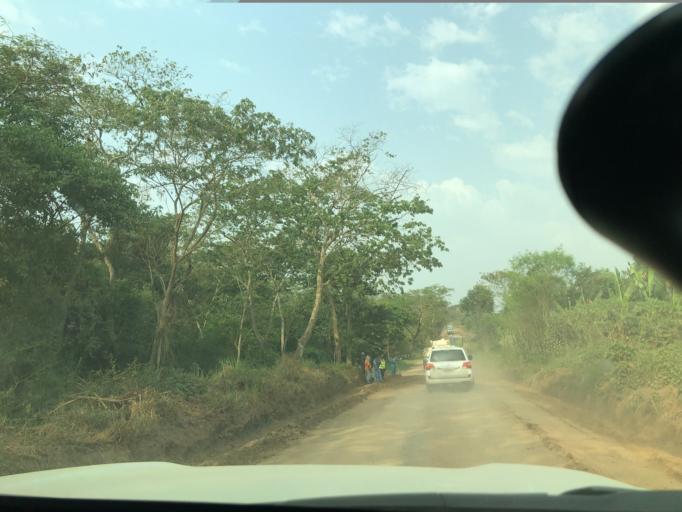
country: UG
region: Western Region
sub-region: Kasese District
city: Margherita
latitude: 0.1945
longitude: 29.6580
